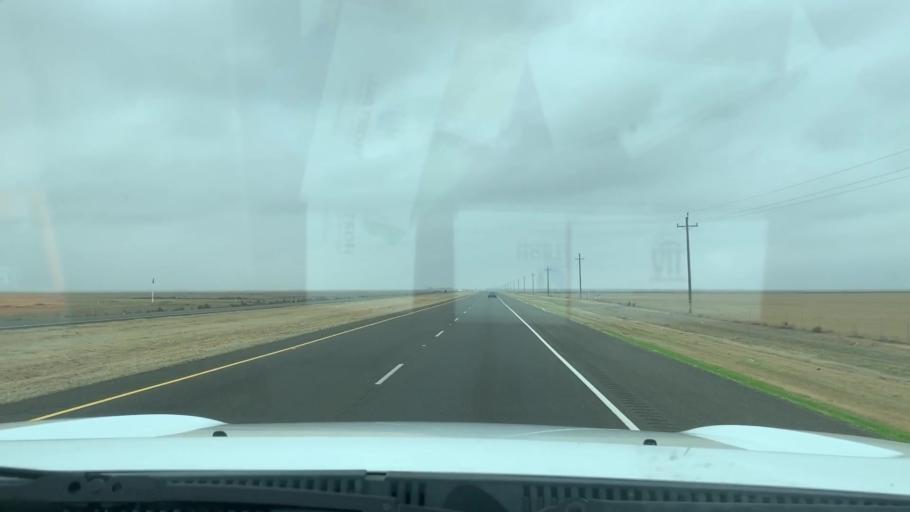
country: US
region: California
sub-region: Kern County
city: Lost Hills
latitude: 35.6158
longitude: -119.7990
